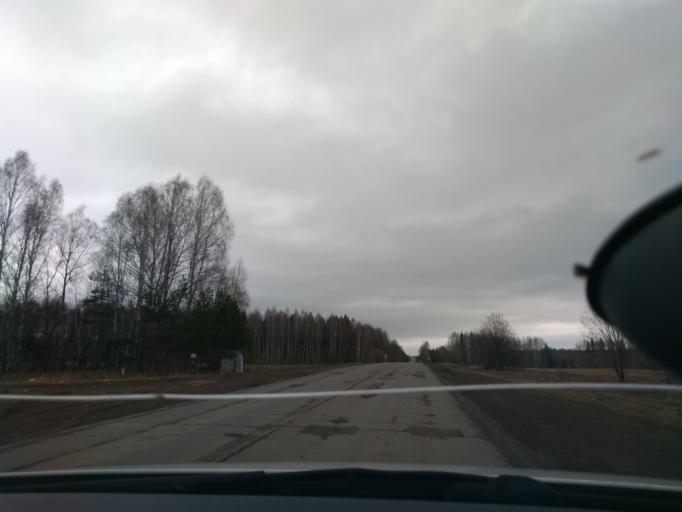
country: RU
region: Perm
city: Kungur
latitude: 57.3636
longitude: 56.8215
